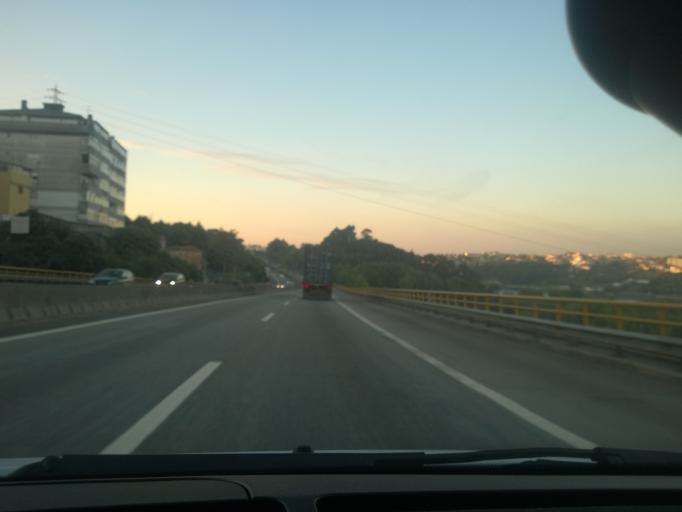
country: PT
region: Porto
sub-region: Vila Nova de Gaia
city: Oliveira do Douro
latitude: 41.1174
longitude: -8.5719
